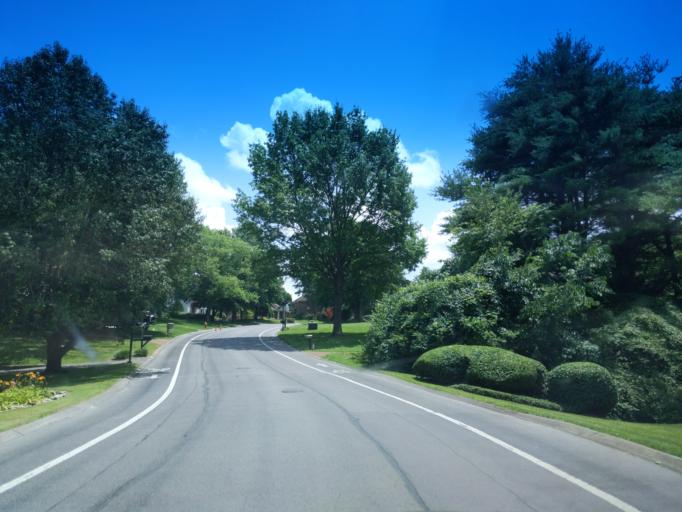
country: US
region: Tennessee
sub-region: Williamson County
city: Brentwood
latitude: 36.0431
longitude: -86.7621
